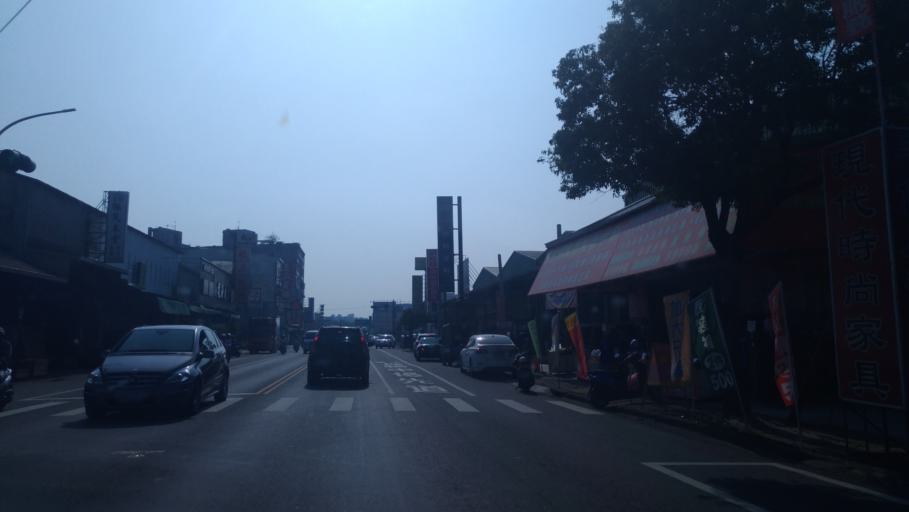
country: TW
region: Taiwan
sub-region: Chiayi
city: Jiayi Shi
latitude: 23.4979
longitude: 120.4421
